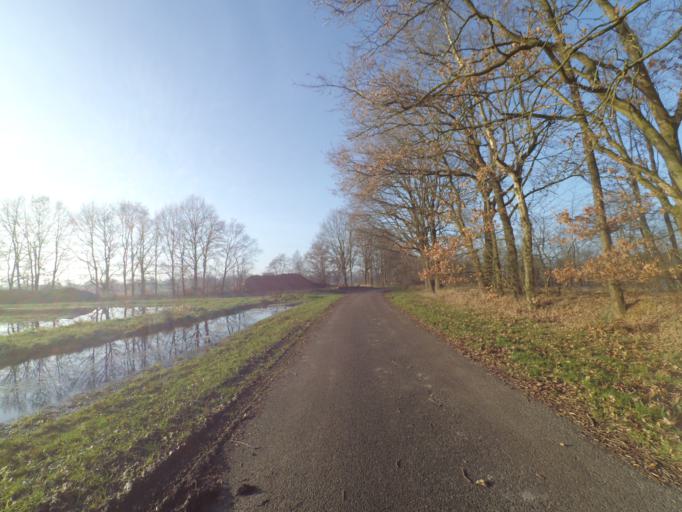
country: NL
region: Drenthe
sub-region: Gemeente Borger-Odoorn
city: Borger
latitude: 52.8797
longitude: 6.6626
